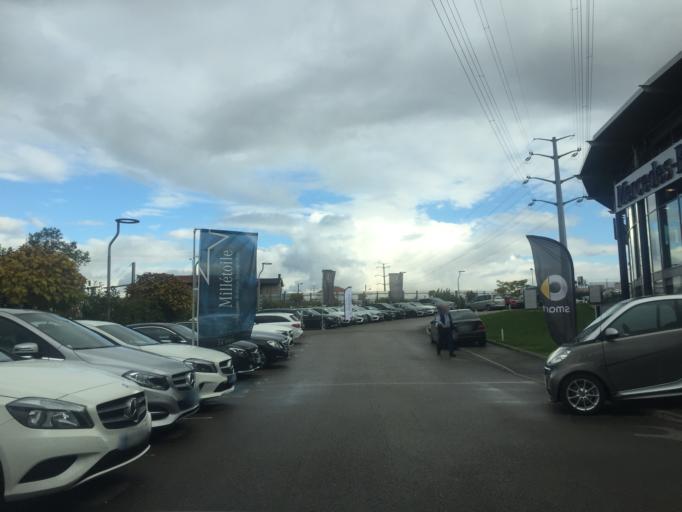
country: FR
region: Rhone-Alpes
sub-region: Departement du Rhone
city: Saint-Fons
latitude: 45.7155
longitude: 4.8533
